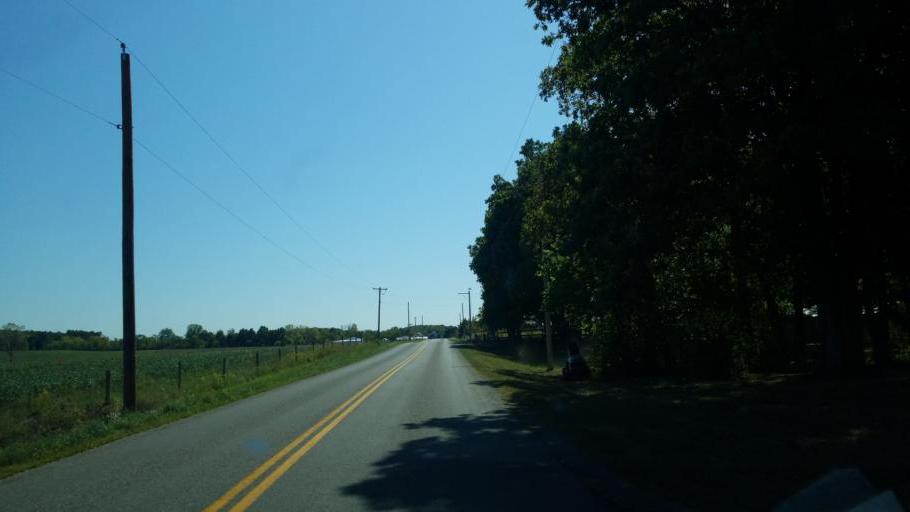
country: US
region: Ohio
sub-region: Logan County
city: Northwood
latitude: 40.4505
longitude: -83.7902
